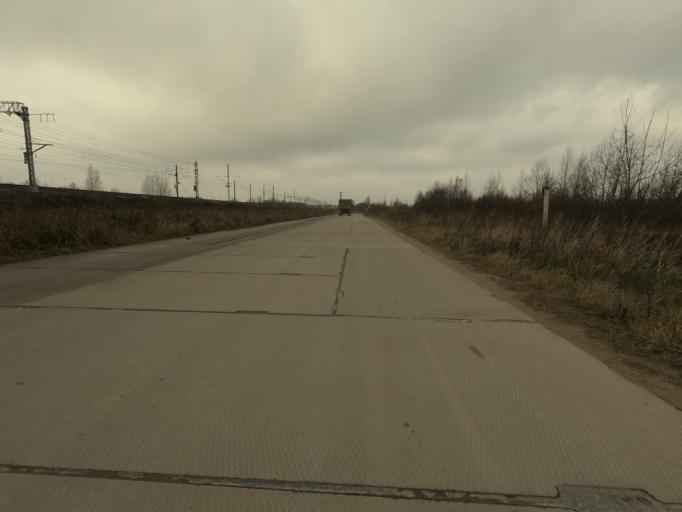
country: RU
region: Leningrad
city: Lyuban'
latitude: 59.4779
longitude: 31.2579
